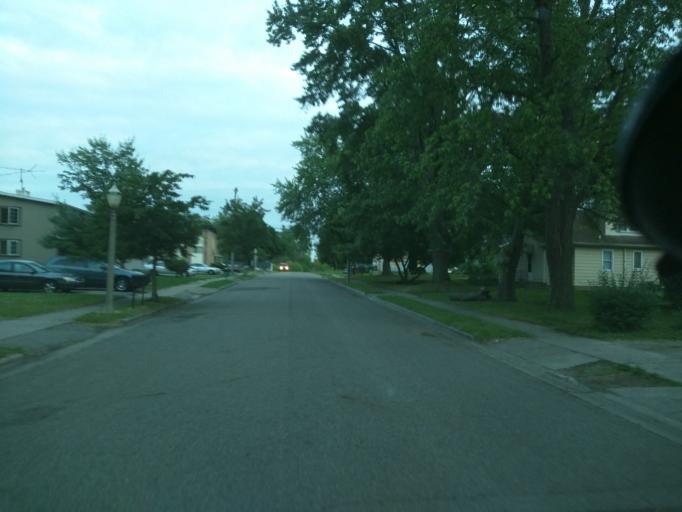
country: US
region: Michigan
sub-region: Ingham County
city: Lansing
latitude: 42.6988
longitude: -84.5837
